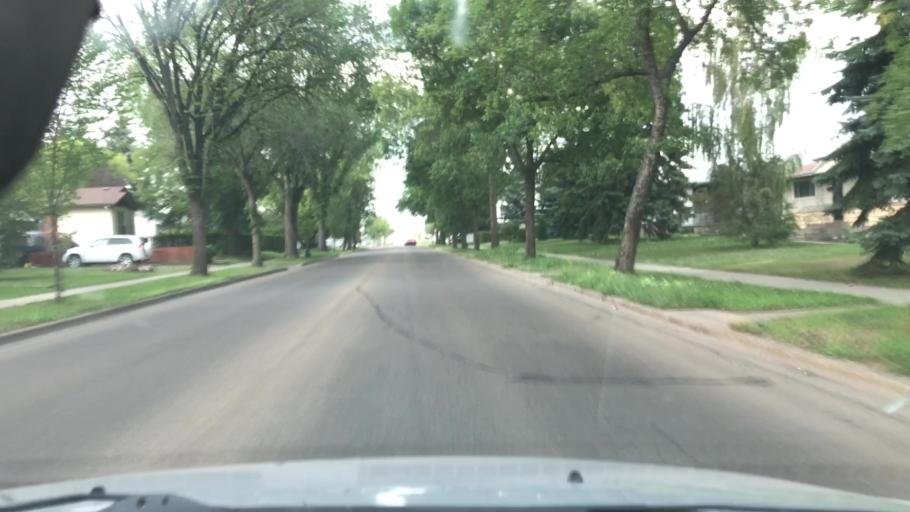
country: CA
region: Alberta
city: Edmonton
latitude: 53.5882
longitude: -113.5165
